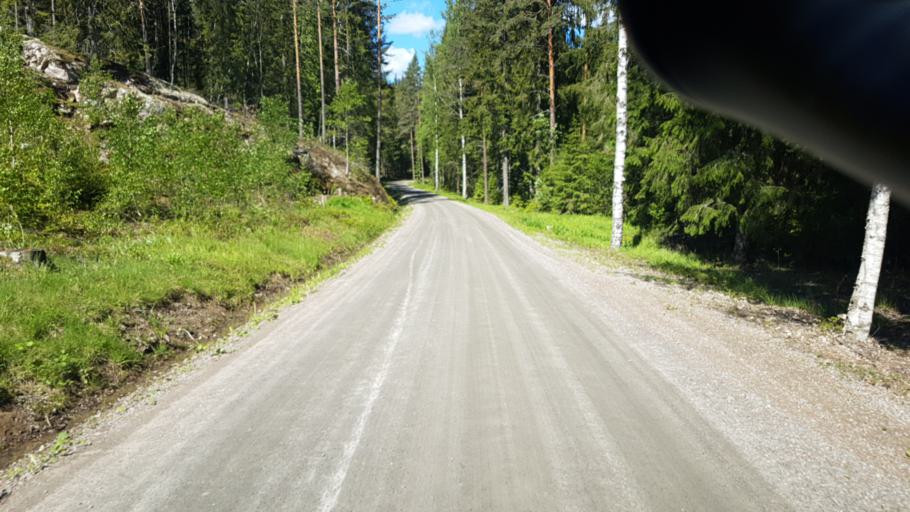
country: SE
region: Vaermland
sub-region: Arvika Kommun
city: Arvika
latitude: 59.5971
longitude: 12.7938
